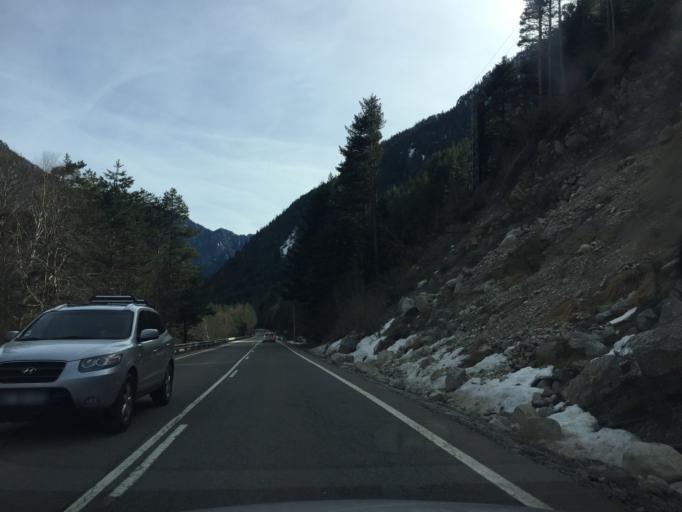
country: ES
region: Aragon
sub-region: Provincia de Huesca
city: Bielsa
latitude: 42.6958
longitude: 0.2025
